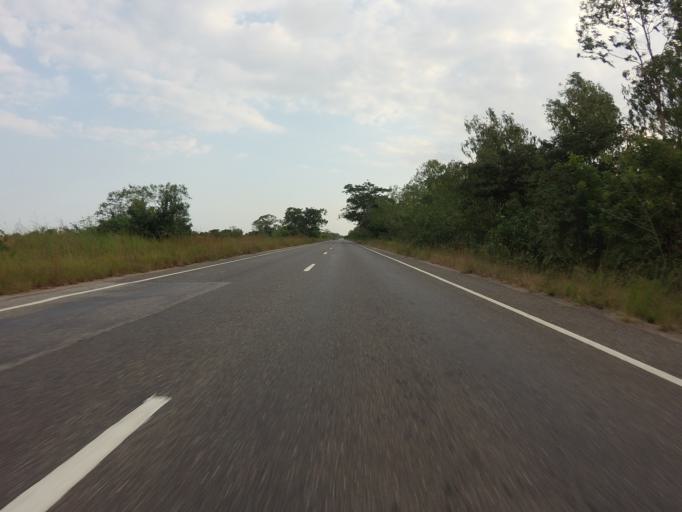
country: GH
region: Volta
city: Ho
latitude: 6.1199
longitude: 0.5202
